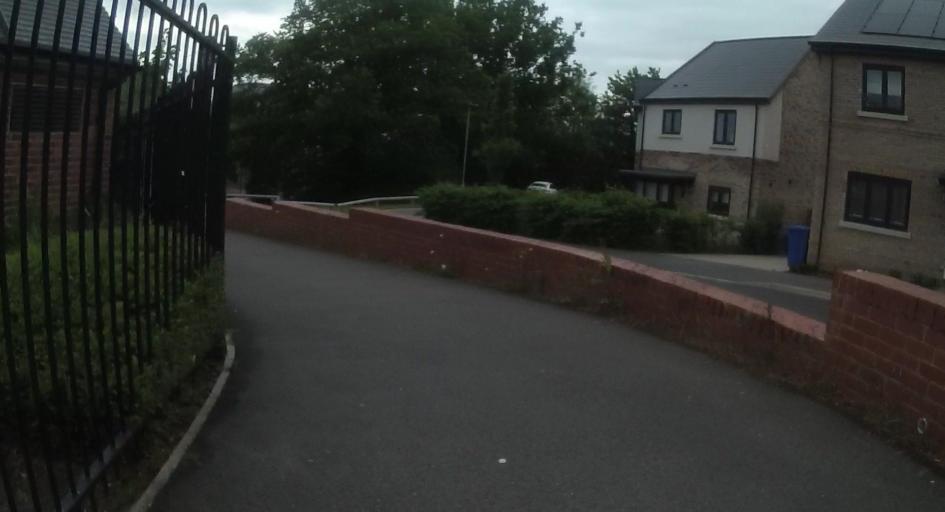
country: GB
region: England
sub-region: Bracknell Forest
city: Bracknell
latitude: 51.4213
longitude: -0.7485
